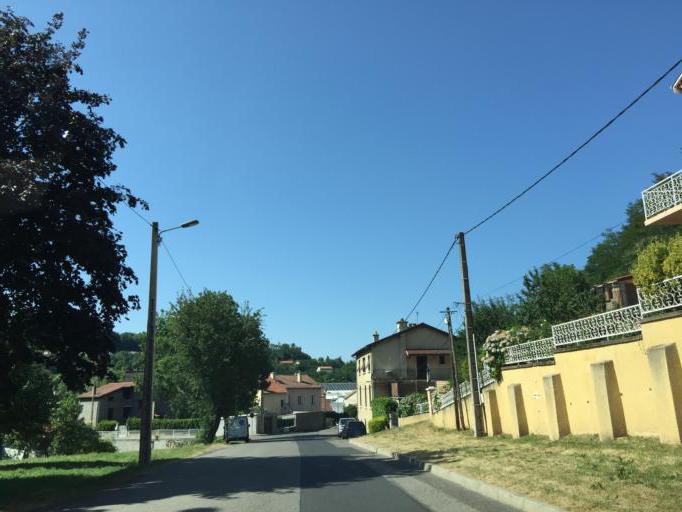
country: FR
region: Rhone-Alpes
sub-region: Departement de la Loire
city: Saint-Jean-Bonnefonds
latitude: 45.4303
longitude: 4.4344
